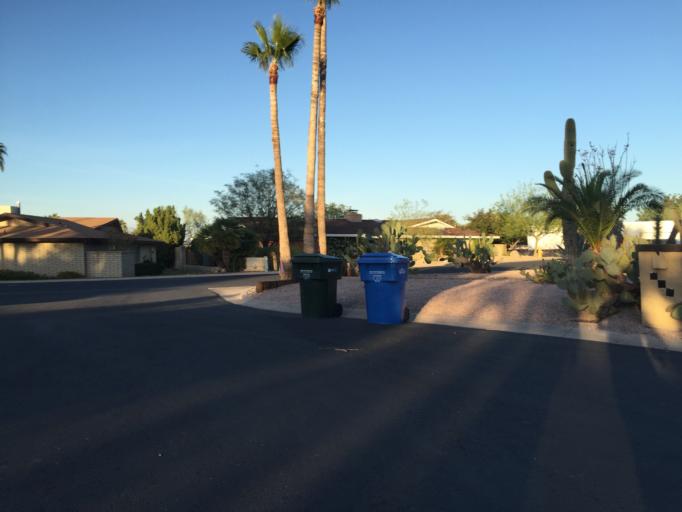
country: US
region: Arizona
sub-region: Maricopa County
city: Paradise Valley
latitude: 33.5681
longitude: -112.0166
